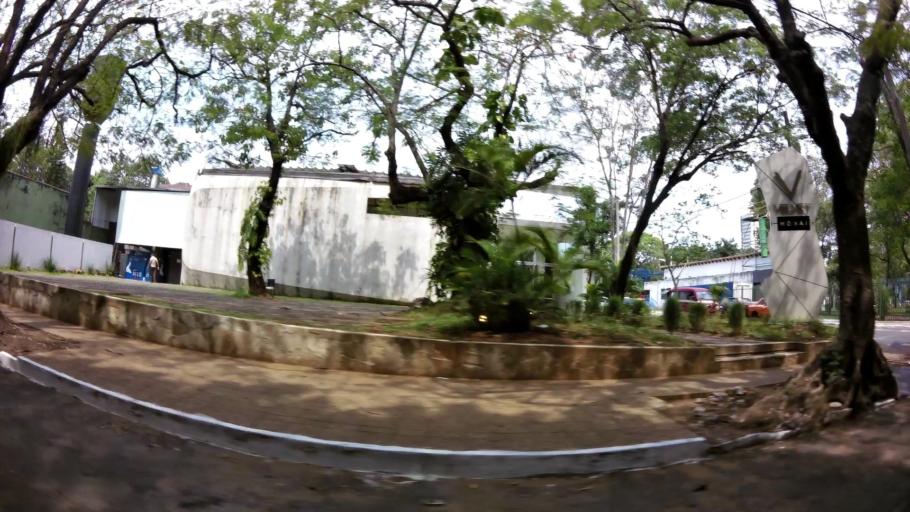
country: PY
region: Asuncion
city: Asuncion
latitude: -25.2942
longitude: -57.5775
